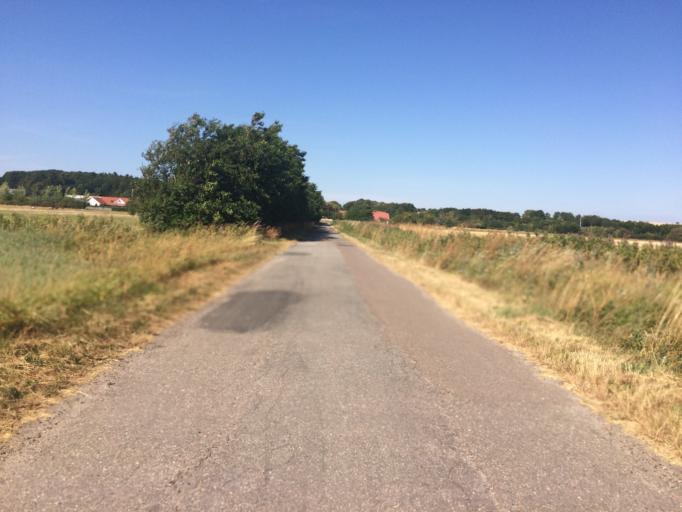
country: DK
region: Central Jutland
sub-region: Holstebro Kommune
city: Vinderup
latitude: 56.5797
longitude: 8.8260
